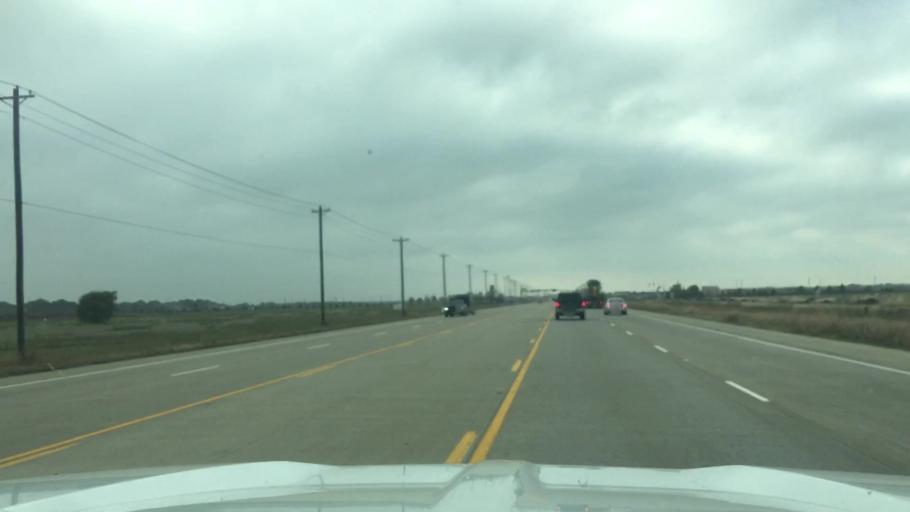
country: US
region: Texas
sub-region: Collin County
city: Prosper
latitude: 33.2192
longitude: -96.8671
